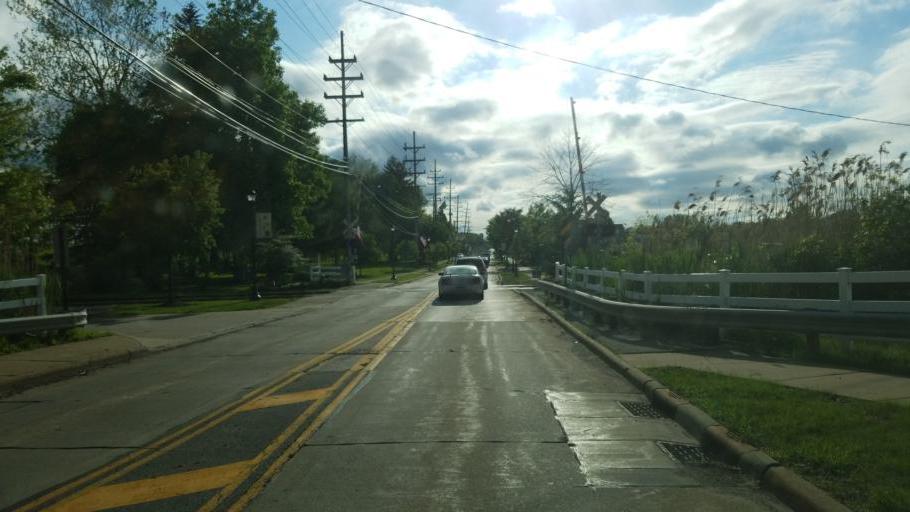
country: US
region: Ohio
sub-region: Cuyahoga County
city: Solon
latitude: 41.3569
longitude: -81.4664
